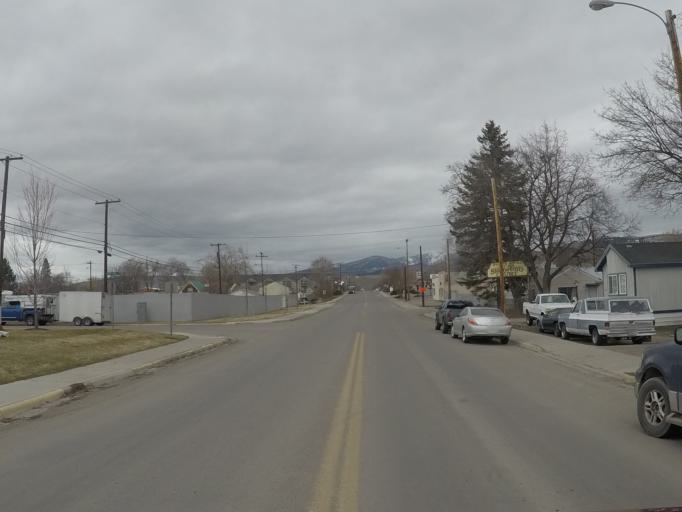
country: US
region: Montana
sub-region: Missoula County
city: Missoula
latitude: 46.8794
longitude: -114.0185
